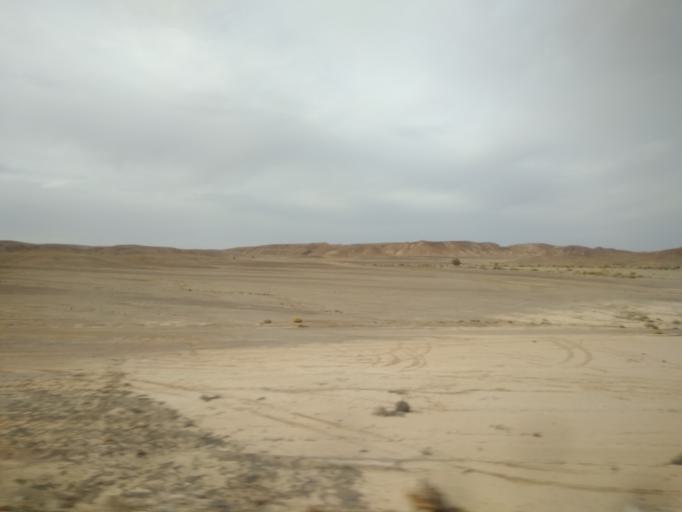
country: IL
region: Southern District
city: Eilat
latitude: 29.9099
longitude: 34.8728
